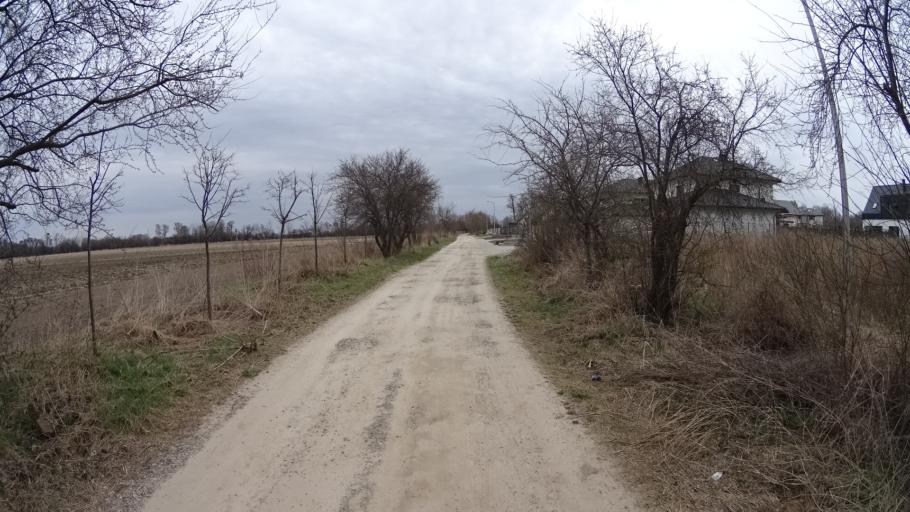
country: PL
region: Masovian Voivodeship
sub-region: Powiat warszawski zachodni
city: Ozarow Mazowiecki
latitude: 52.2357
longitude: 20.7856
